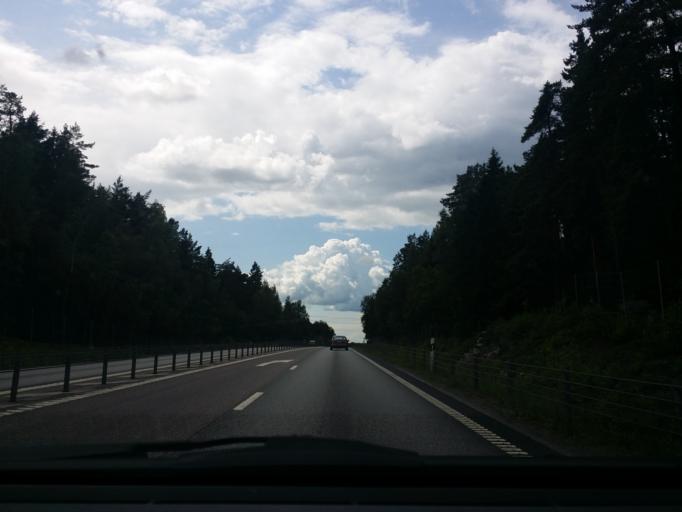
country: SE
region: Vaestmanland
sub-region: Kopings Kommun
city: Koping
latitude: 59.5430
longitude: 16.0073
